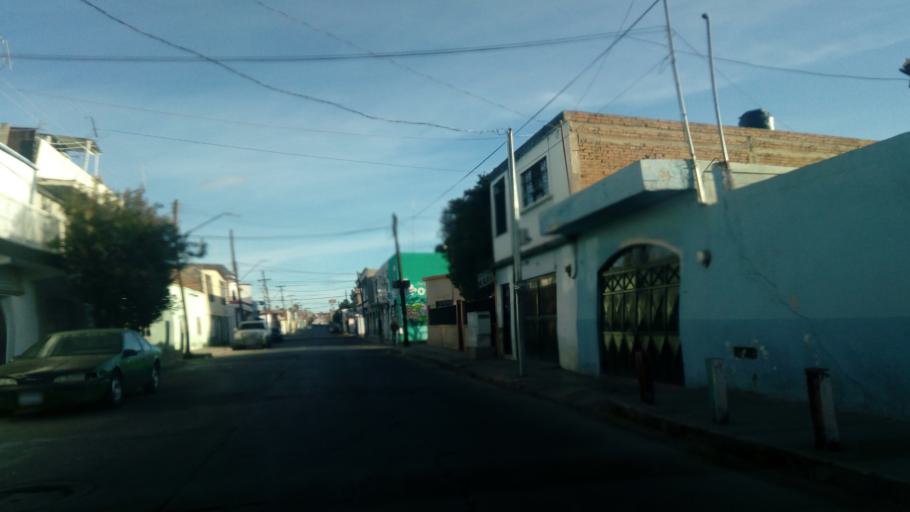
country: MX
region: Durango
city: Victoria de Durango
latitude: 24.0076
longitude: -104.6767
